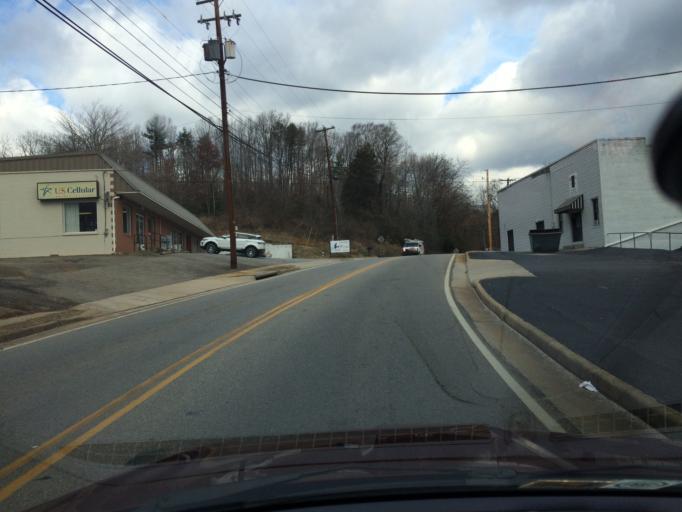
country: US
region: Virginia
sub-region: Patrick County
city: Stuart
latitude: 36.6367
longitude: -80.2700
